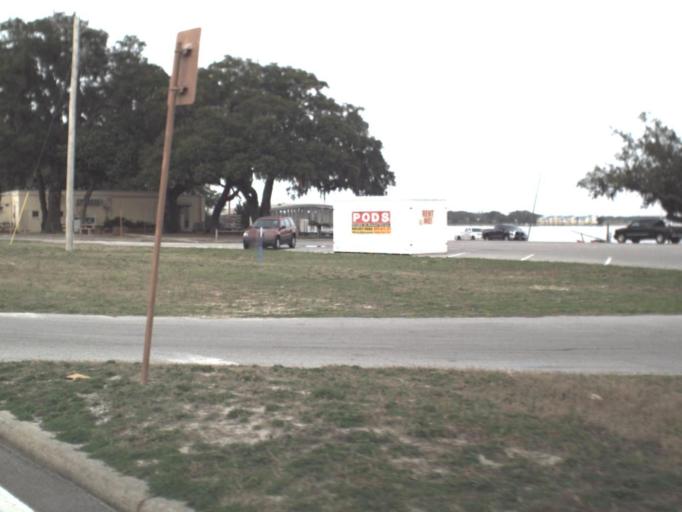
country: US
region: Florida
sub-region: Bay County
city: Tyndall Air Force Base
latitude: 30.0977
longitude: -85.6125
